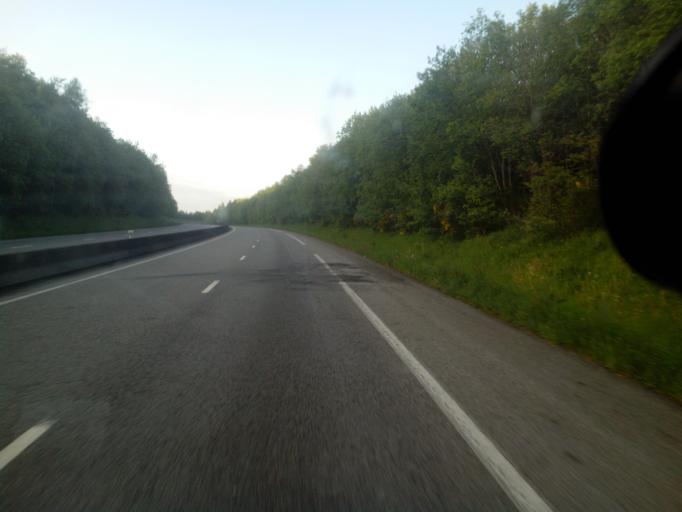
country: FR
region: Haute-Normandie
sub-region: Departement de la Seine-Maritime
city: Foucarmont
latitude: 49.8854
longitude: 1.5989
